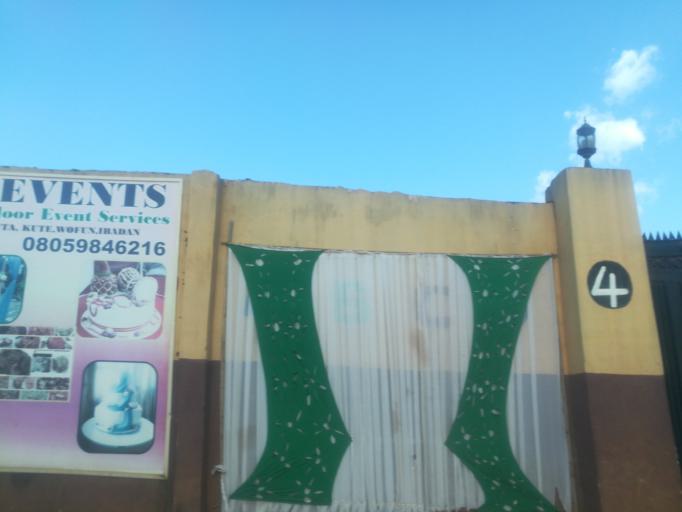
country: NG
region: Oyo
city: Lalupon
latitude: 7.4403
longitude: 3.9813
